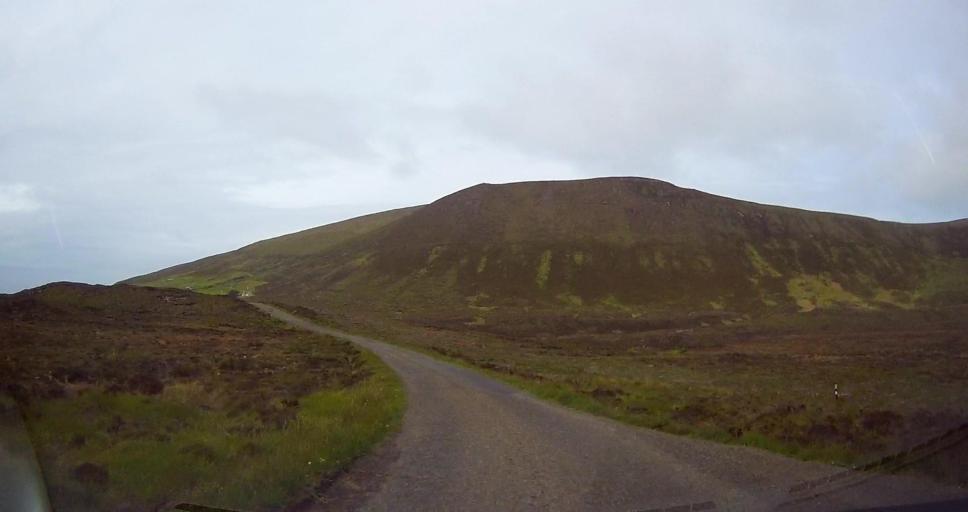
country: GB
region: Scotland
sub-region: Orkney Islands
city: Stromness
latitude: 58.8825
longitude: -3.3793
